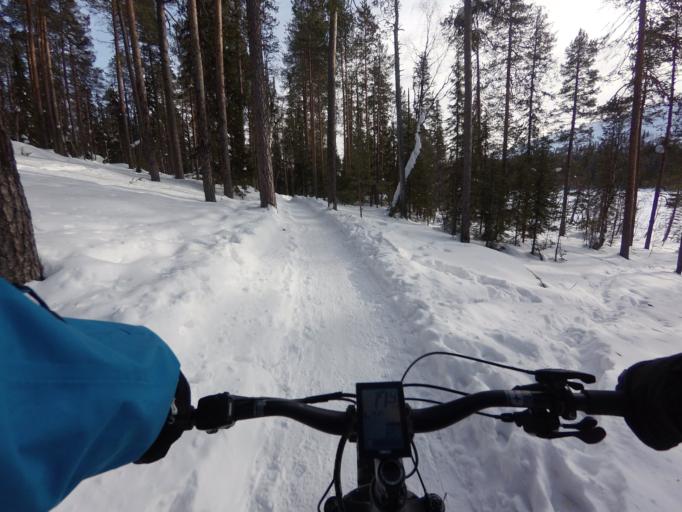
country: FI
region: Lapland
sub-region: Tunturi-Lappi
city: Kolari
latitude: 67.6000
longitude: 24.2460
